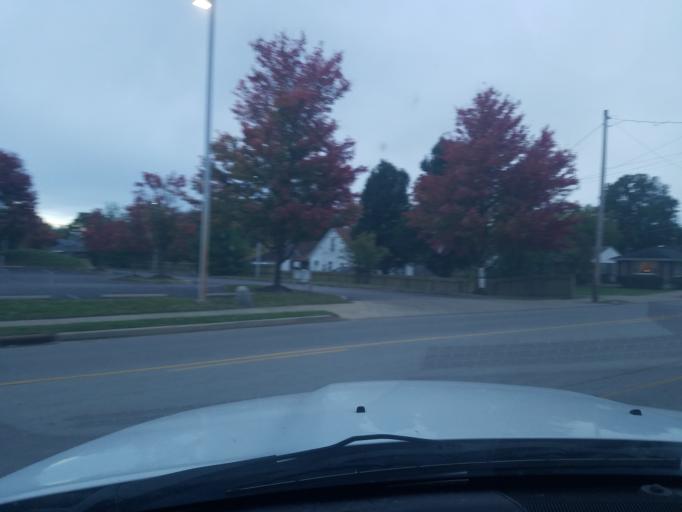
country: US
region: Indiana
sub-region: Floyd County
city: New Albany
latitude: 38.3056
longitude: -85.8366
